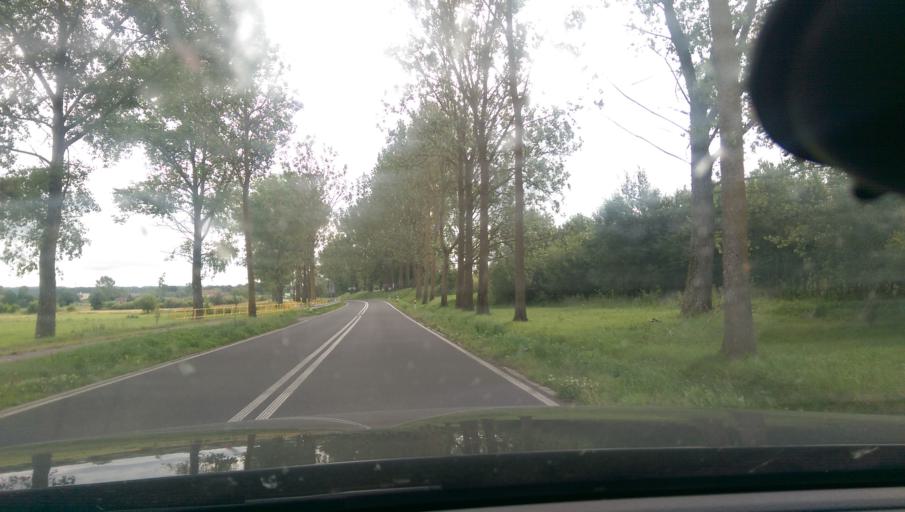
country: PL
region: Warmian-Masurian Voivodeship
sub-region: Powiat goldapski
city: Banie Mazurskie
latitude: 54.2441
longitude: 22.0194
